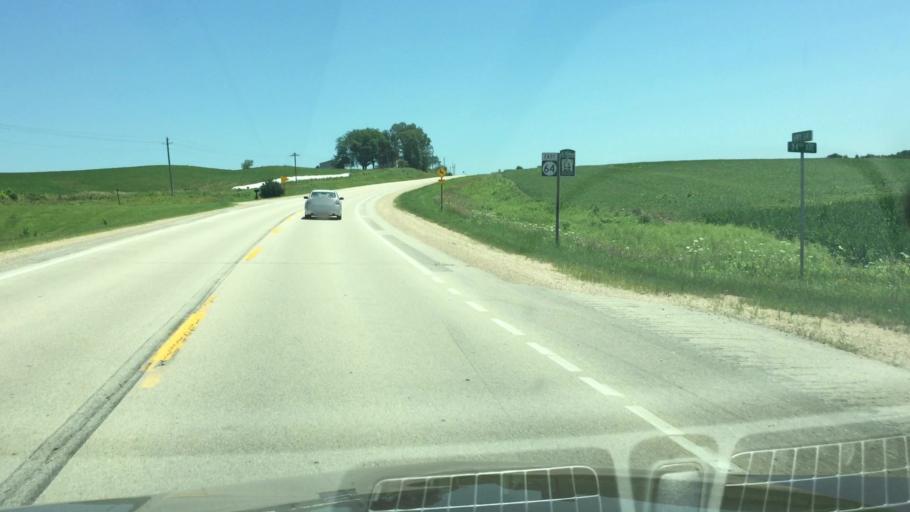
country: US
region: Iowa
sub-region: Jackson County
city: Maquoketa
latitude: 42.0727
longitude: -90.8007
